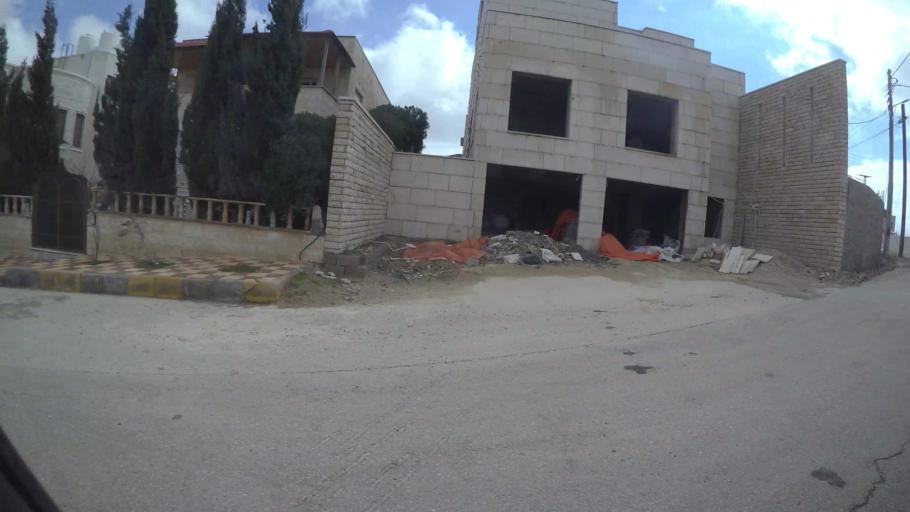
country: JO
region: Amman
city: Al Jubayhah
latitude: 32.0757
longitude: 35.8834
